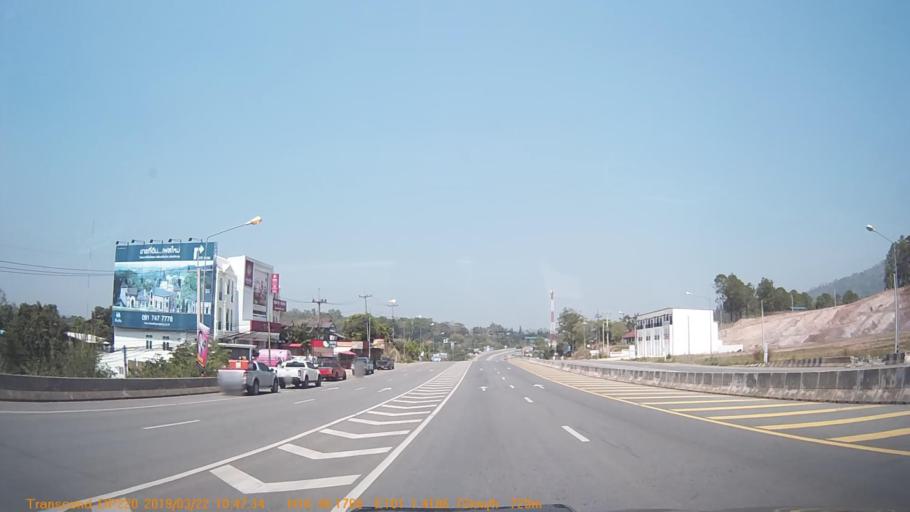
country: TH
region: Phetchabun
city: Khao Kho
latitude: 16.7697
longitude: 101.0234
